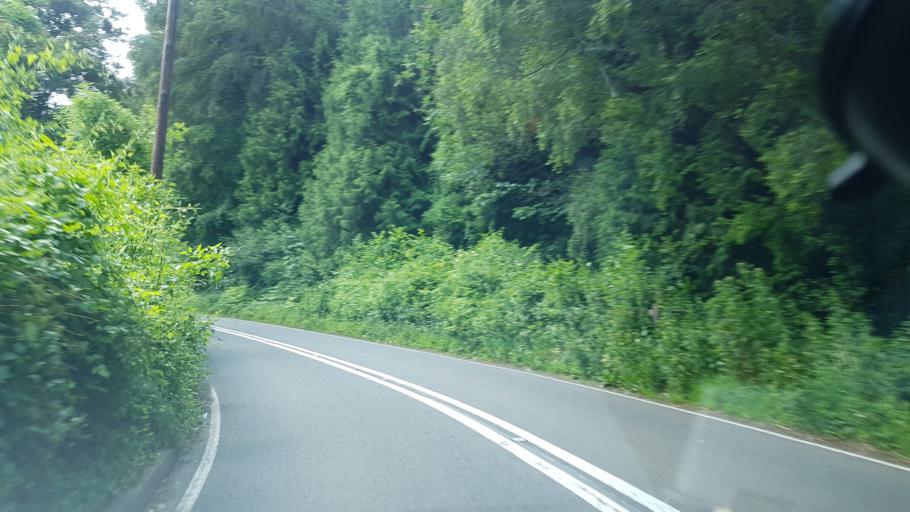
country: GB
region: Wales
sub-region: Monmouthshire
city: Chepstow
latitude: 51.6449
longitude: -2.7219
